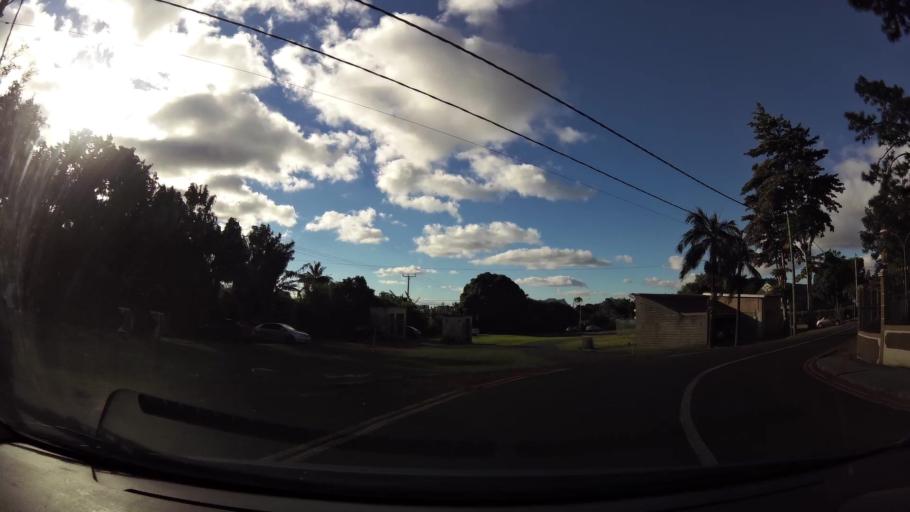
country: MU
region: Plaines Wilhems
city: Vacoas
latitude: -20.2920
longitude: 57.4942
